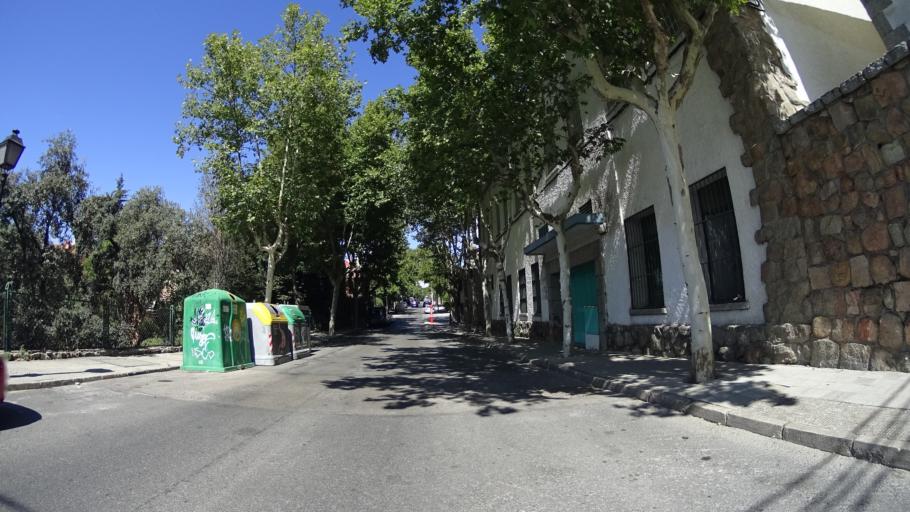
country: ES
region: Madrid
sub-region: Provincia de Madrid
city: Torrelodones
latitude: 40.5749
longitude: -3.9539
